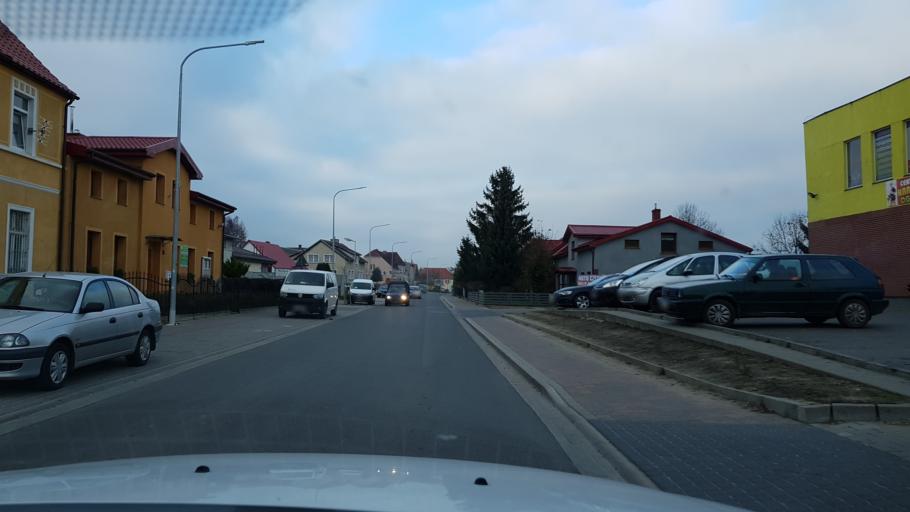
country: PL
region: West Pomeranian Voivodeship
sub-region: Powiat kolobrzeski
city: Goscino
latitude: 54.0500
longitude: 15.6539
